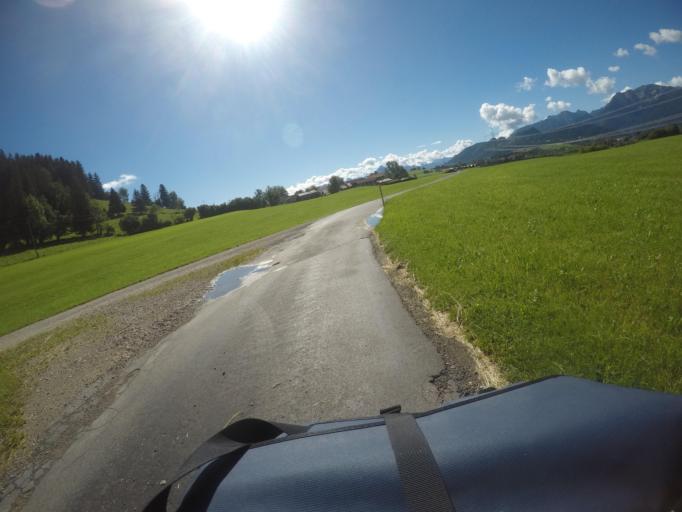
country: DE
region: Bavaria
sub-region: Swabia
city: Pfronten
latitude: 47.6068
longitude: 10.5541
